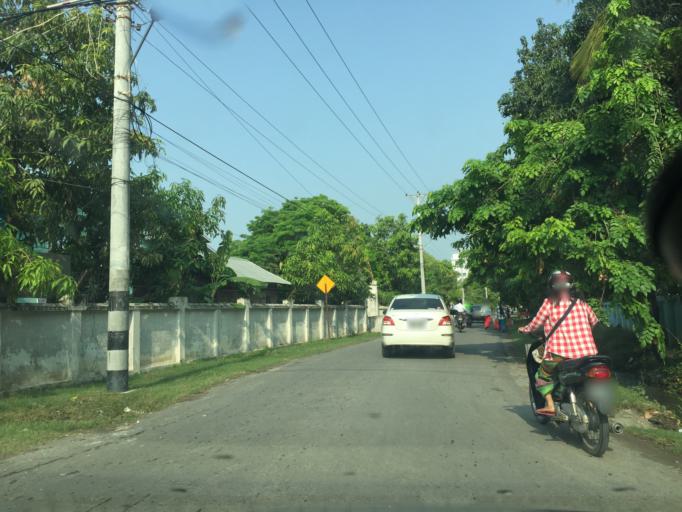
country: MM
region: Mandalay
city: Mandalay
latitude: 21.9730
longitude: 96.1002
